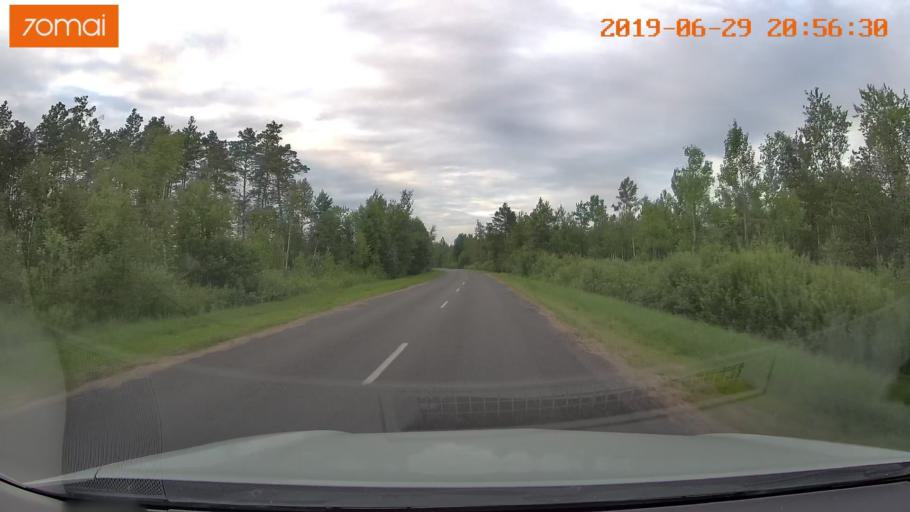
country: BY
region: Brest
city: Hantsavichy
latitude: 52.7063
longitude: 26.3680
